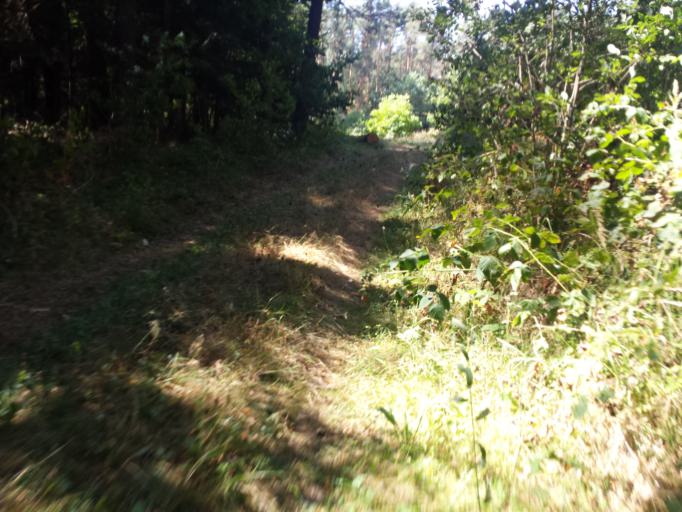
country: PL
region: Swietokrzyskie
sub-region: Powiat kielecki
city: Daleszyce
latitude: 50.8029
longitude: 20.7589
